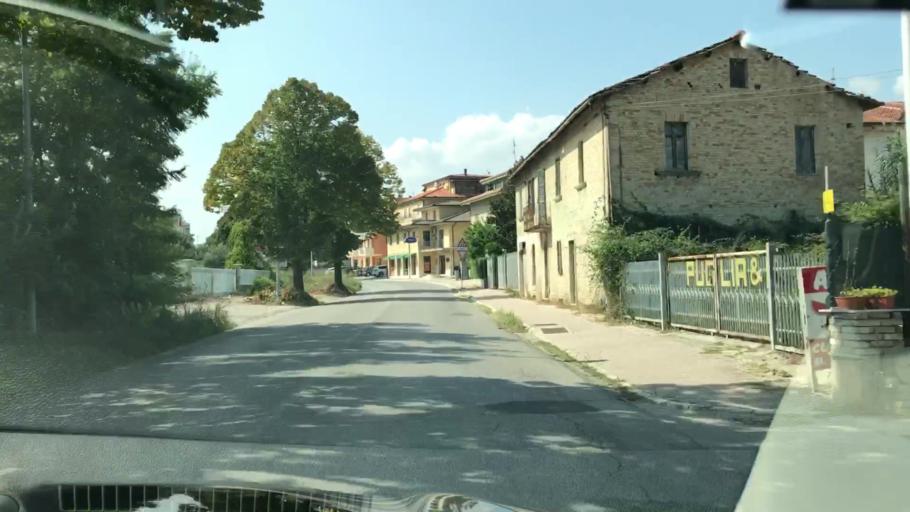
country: IT
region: The Marches
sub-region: Provincia di Ascoli Piceno
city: Pagliare
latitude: 42.8745
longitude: 13.7699
